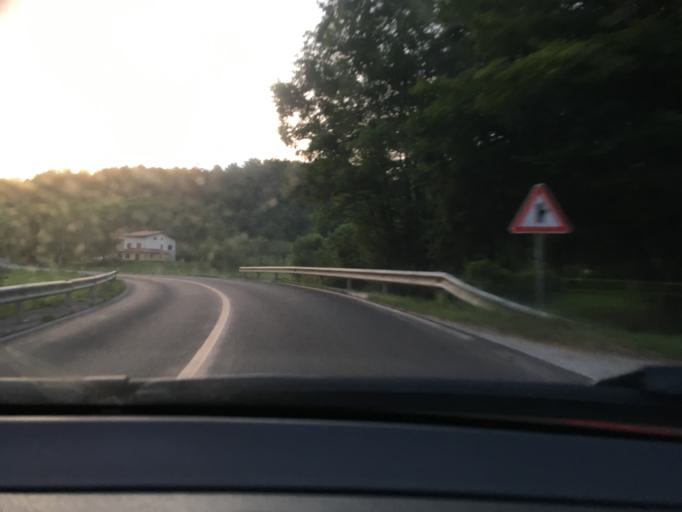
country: SI
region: Pivka
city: Pivka
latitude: 45.6090
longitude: 14.1887
